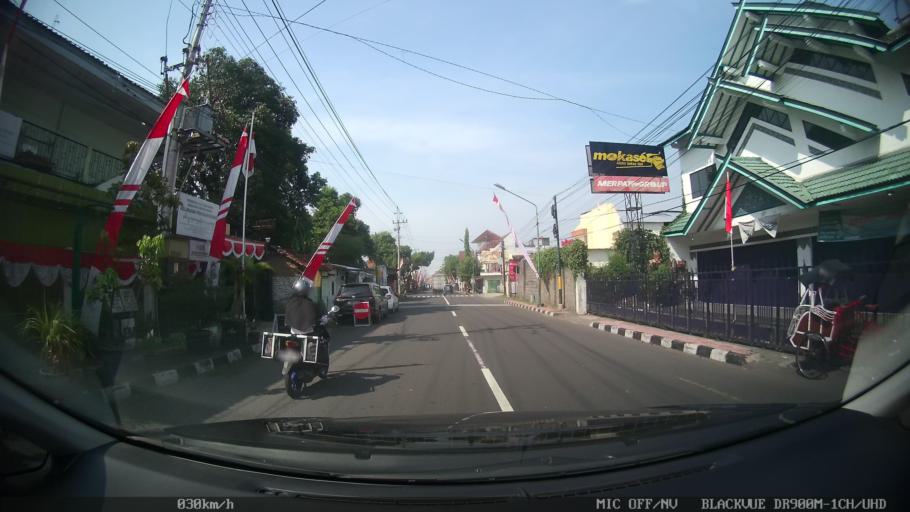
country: ID
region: Daerah Istimewa Yogyakarta
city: Yogyakarta
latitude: -7.7922
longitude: 110.3571
